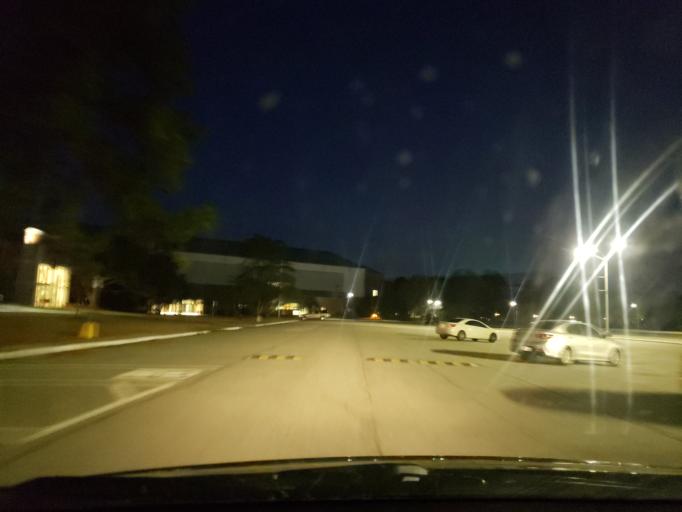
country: US
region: Georgia
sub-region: Chatham County
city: Montgomery
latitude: 31.9782
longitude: -81.1616
